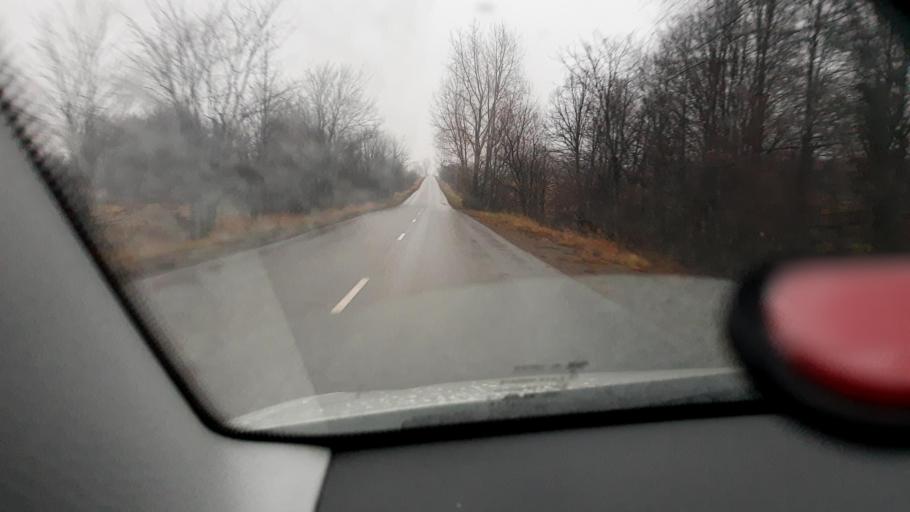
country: RU
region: Bashkortostan
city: Iglino
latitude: 54.8995
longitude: 56.2484
